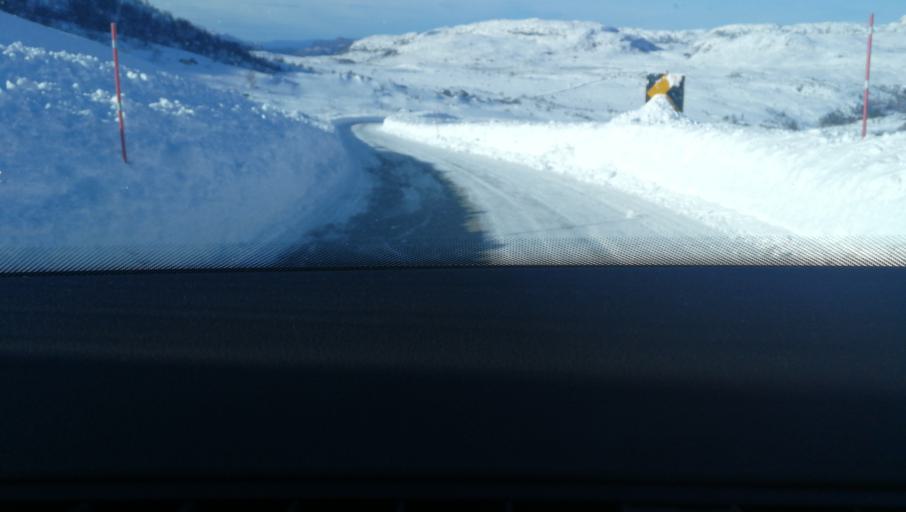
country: NO
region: Rogaland
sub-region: Hjelmeland
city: Hjelmelandsvagen
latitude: 59.1021
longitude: 6.3839
